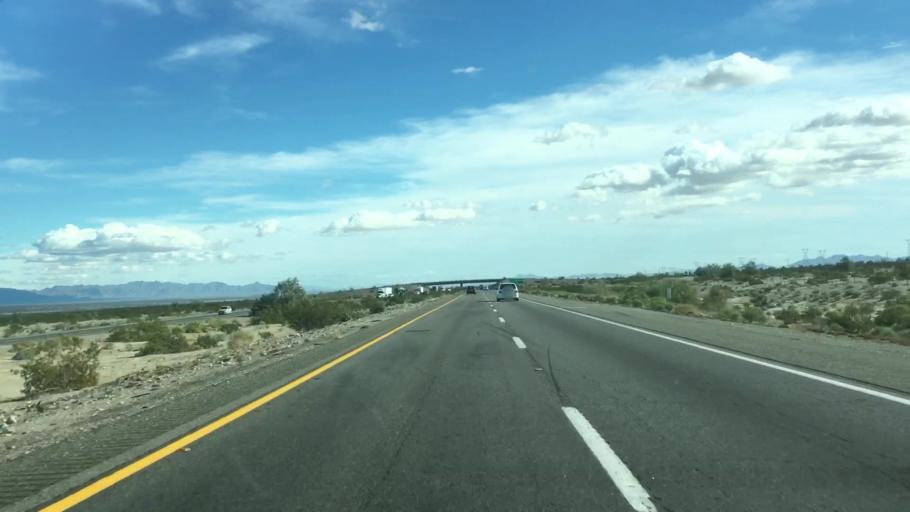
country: US
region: California
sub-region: Imperial County
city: Niland
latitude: 33.6844
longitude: -115.2503
